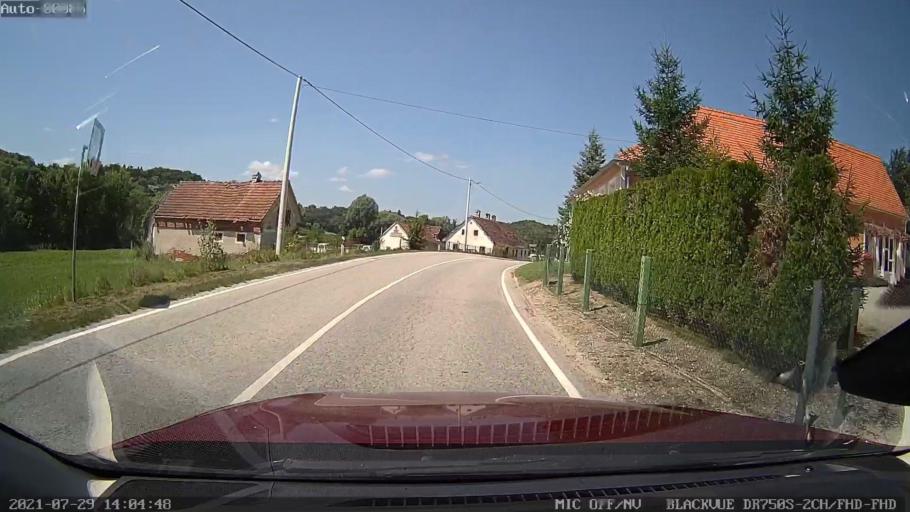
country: HR
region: Varazdinska
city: Lepoglava
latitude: 46.2448
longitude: 15.9603
